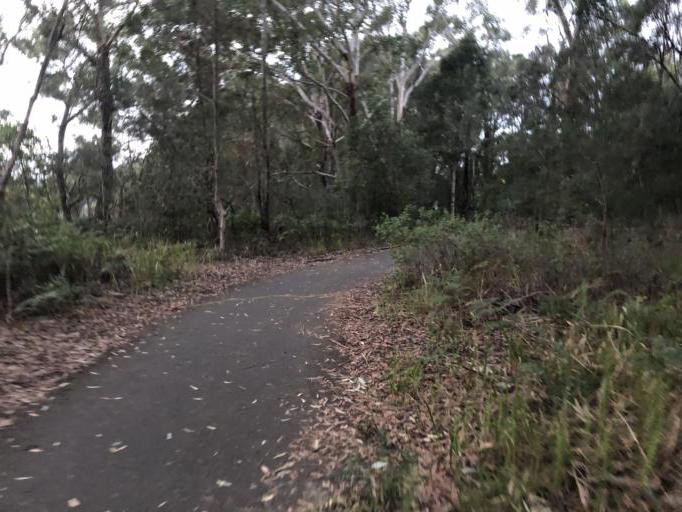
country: AU
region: New South Wales
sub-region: Coffs Harbour
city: Coffs Harbour
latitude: -30.3031
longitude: 153.1272
